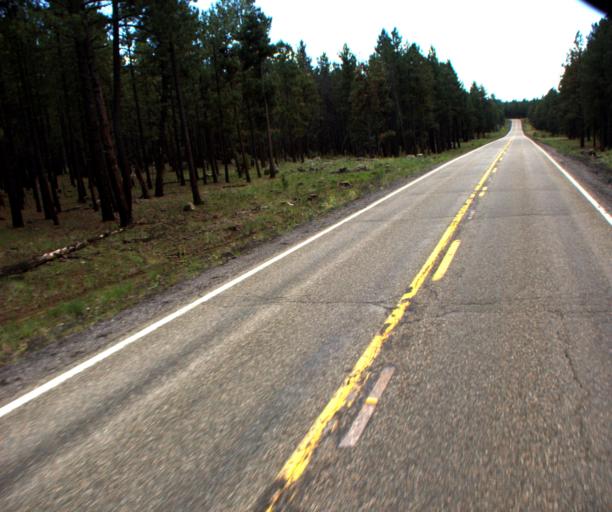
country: US
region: Arizona
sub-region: Coconino County
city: Parks
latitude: 35.3466
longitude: -111.7893
